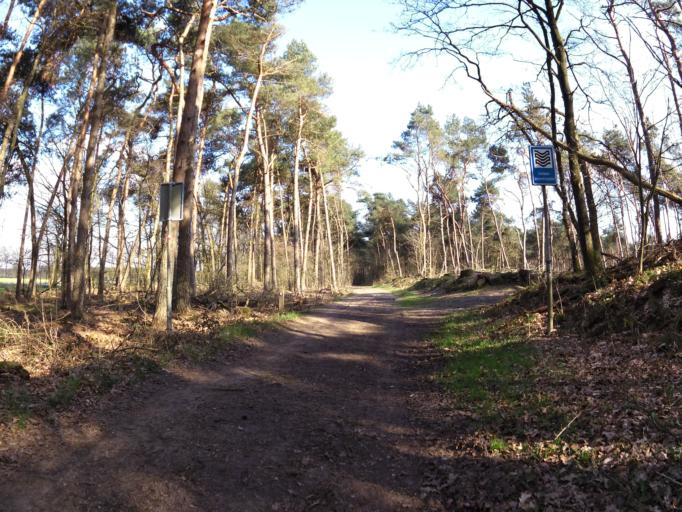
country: NL
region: North Brabant
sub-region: Gemeente Haaren
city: Haaren
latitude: 51.6574
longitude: 5.1652
